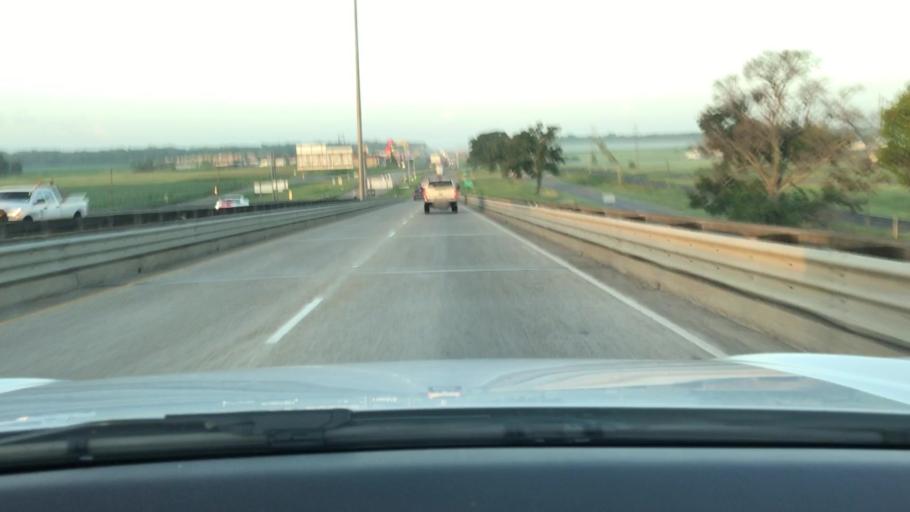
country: US
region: Louisiana
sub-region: West Baton Rouge Parish
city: Port Allen
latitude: 30.4303
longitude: -91.2126
